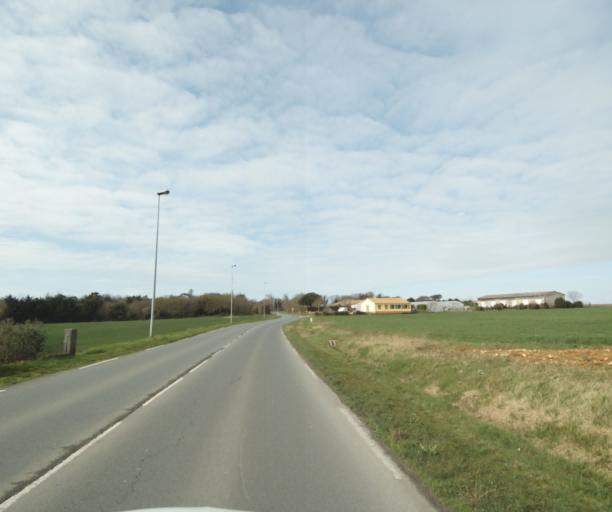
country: FR
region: Poitou-Charentes
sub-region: Departement de la Charente-Maritime
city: Lagord
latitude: 46.1811
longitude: -1.1681
